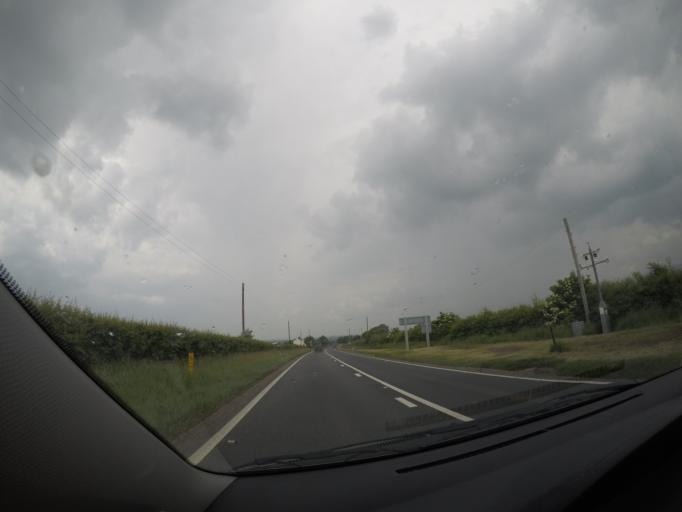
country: GB
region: England
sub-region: Cumbria
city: Appleby-in-Westmorland
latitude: 54.5959
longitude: -2.5327
